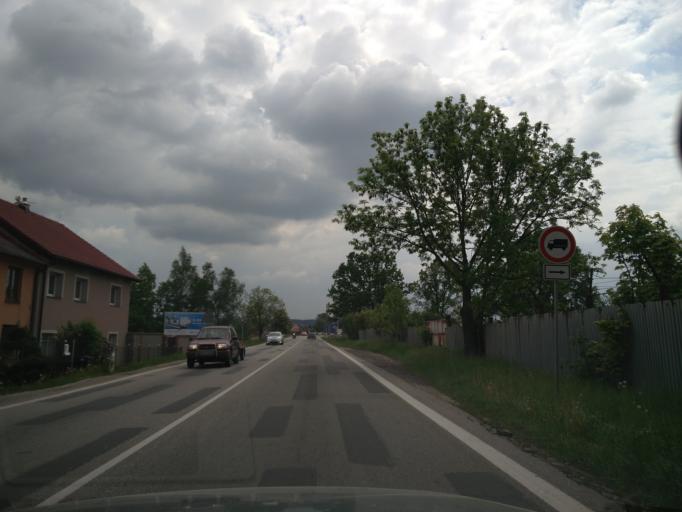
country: CZ
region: Jihocesky
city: Litvinovice
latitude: 48.9496
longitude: 14.4534
